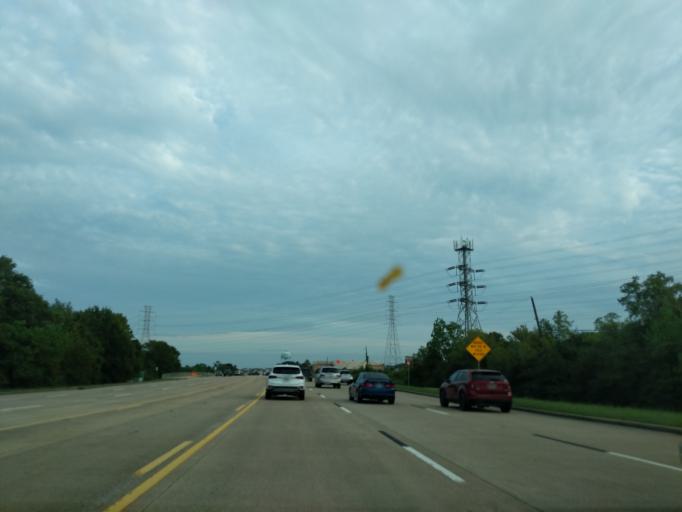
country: US
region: Texas
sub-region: Harris County
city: Nassau Bay
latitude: 29.5299
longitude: -95.0912
